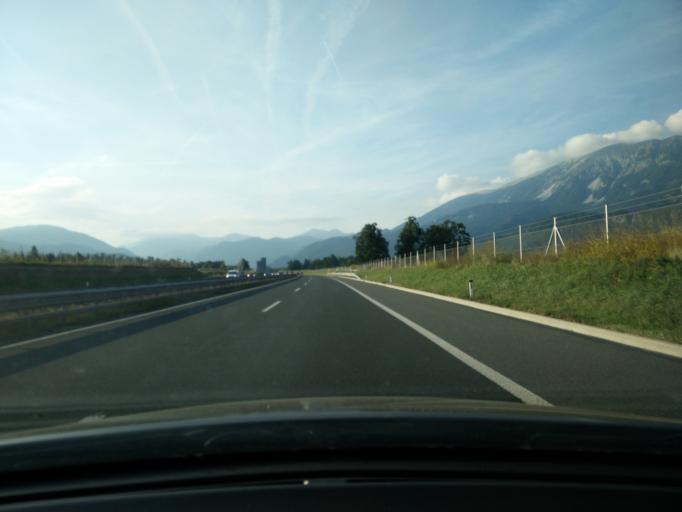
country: SI
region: Radovljica
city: Lesce
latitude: 46.3738
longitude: 14.1564
